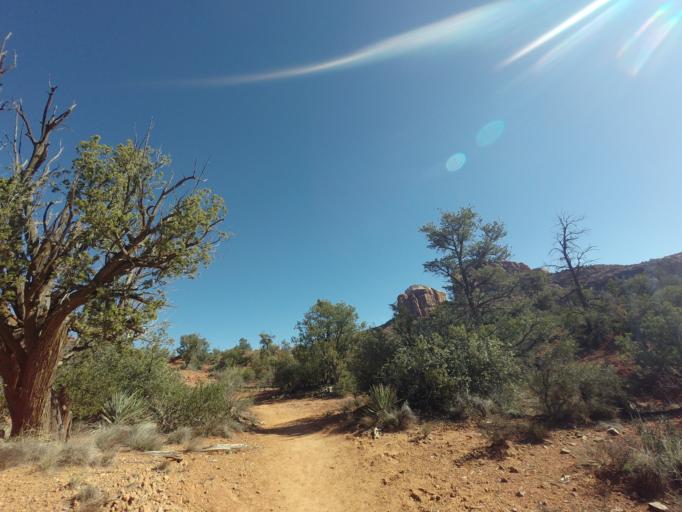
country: US
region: Arizona
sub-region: Yavapai County
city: West Sedona
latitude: 34.8148
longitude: -111.8025
